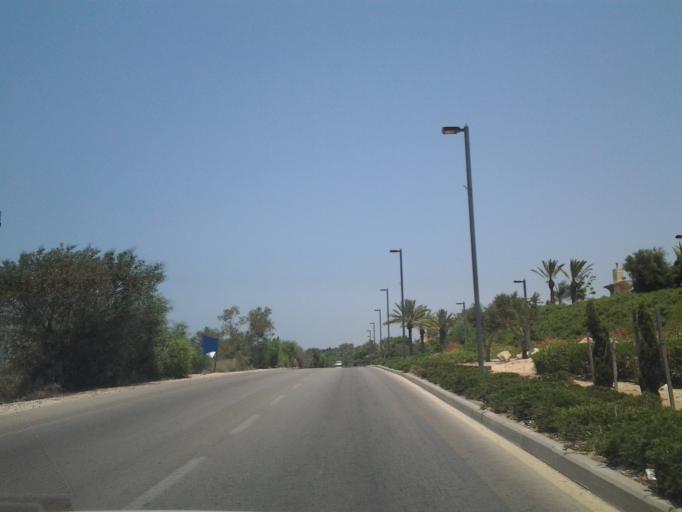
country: IL
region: Haifa
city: Qesarya
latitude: 32.4908
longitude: 34.9035
